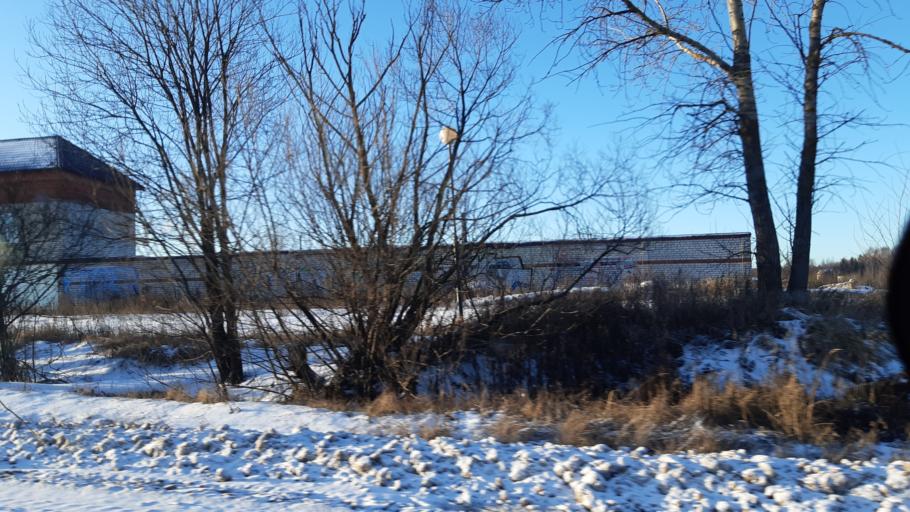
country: RU
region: Moskovskaya
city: Skoropuskovskiy
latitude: 56.3426
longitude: 38.1676
